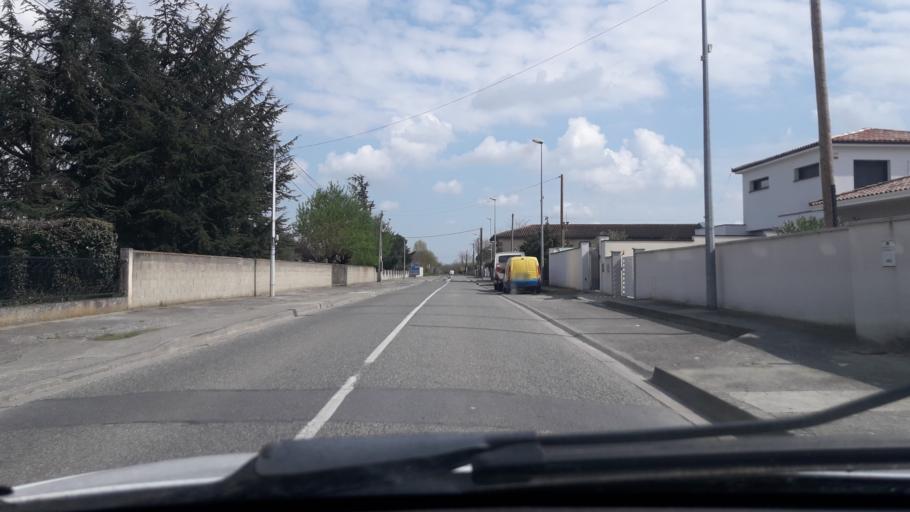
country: FR
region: Midi-Pyrenees
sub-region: Departement de la Haute-Garonne
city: Fonsorbes
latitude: 43.5037
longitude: 1.2583
